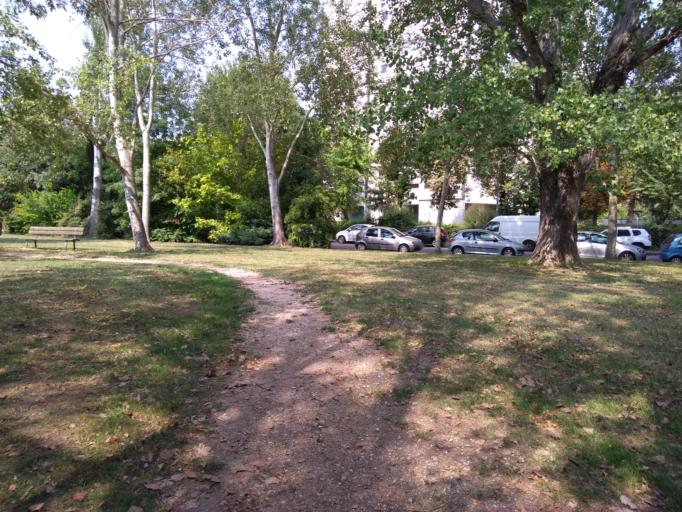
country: IT
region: Emilia-Romagna
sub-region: Provincia di Bologna
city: Quarto Inferiore
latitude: 44.5115
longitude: 11.3921
